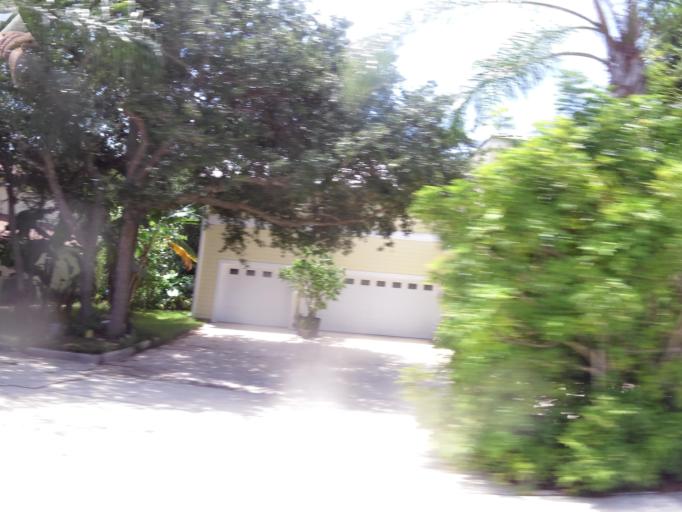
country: US
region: Florida
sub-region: Volusia County
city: Ponce Inlet
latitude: 29.0937
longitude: -80.9377
